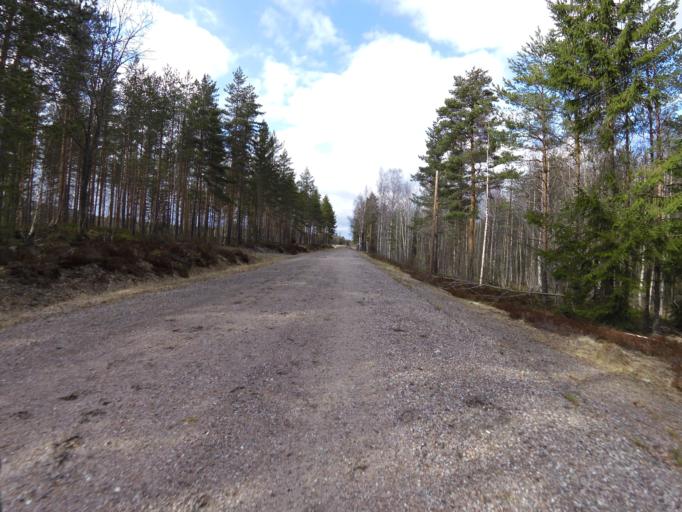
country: SE
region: Gaevleborg
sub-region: Hofors Kommun
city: Hofors
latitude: 60.4830
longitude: 16.4462
